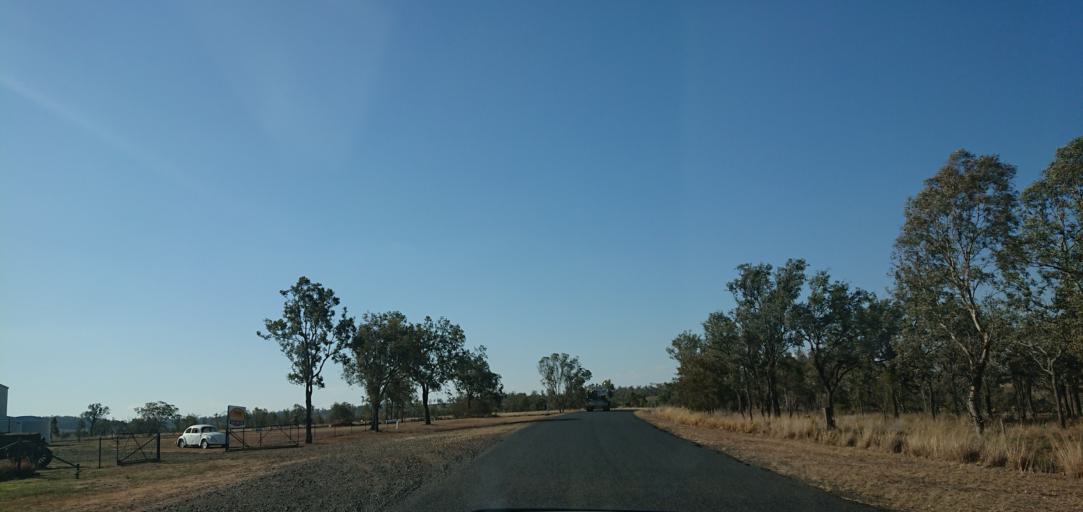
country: AU
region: Queensland
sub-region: Toowoomba
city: Westbrook
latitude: -27.6506
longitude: 151.7259
